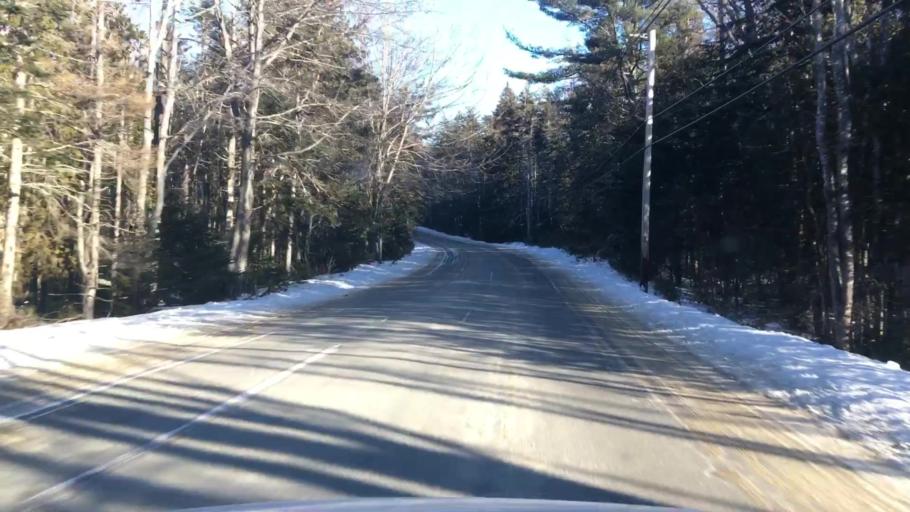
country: US
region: Maine
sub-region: Hancock County
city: Castine
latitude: 44.3597
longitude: -68.7536
